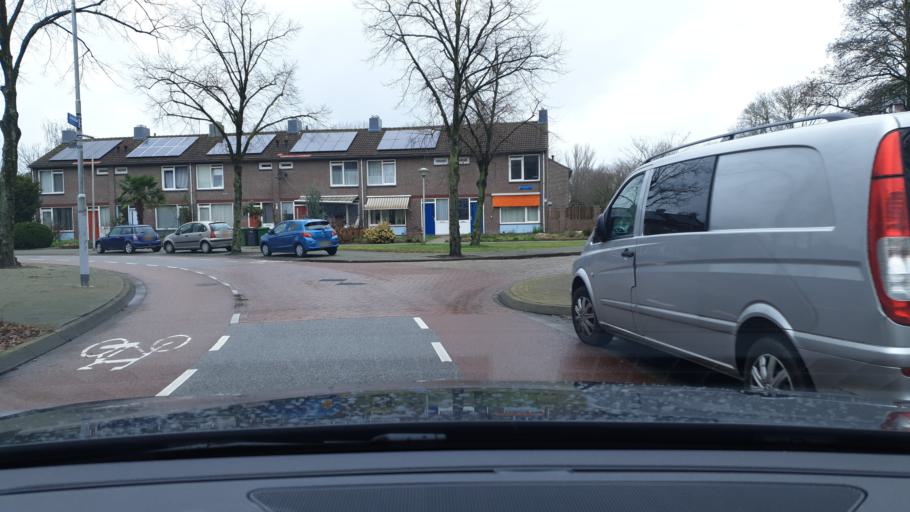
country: NL
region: North Brabant
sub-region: Gemeente Eindhoven
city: Eindhoven
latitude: 51.4279
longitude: 5.4545
